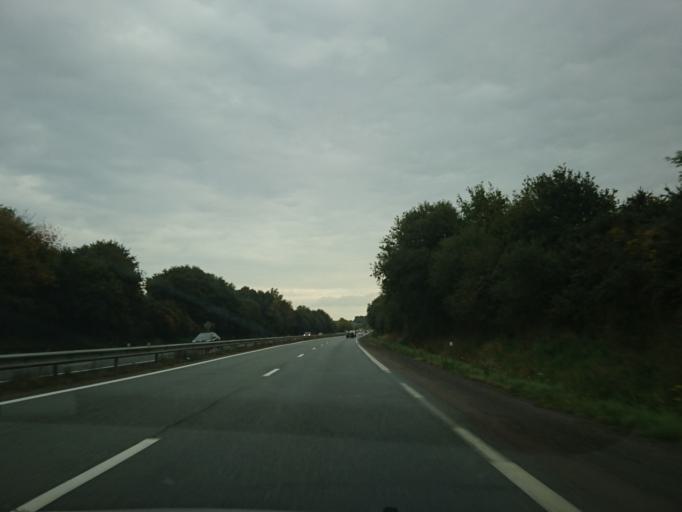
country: FR
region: Brittany
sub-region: Departement des Cotes-d'Armor
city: Caulnes
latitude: 48.2815
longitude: -2.1931
